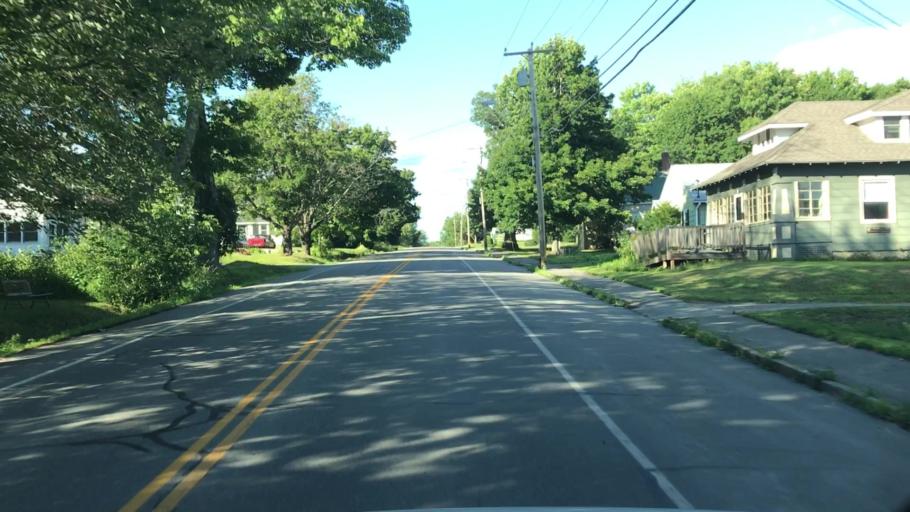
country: US
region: Maine
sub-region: Penobscot County
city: Lincoln
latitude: 45.3692
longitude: -68.4980
